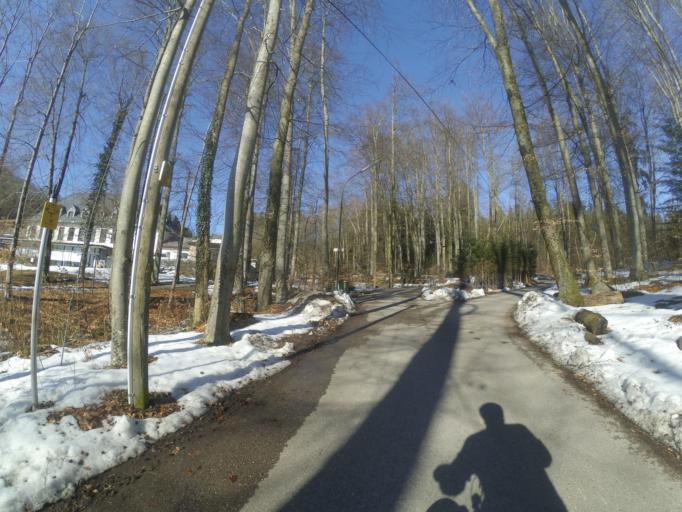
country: DE
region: Bavaria
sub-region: Upper Bavaria
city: Feldkirchen-Westerham
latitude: 47.9072
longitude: 11.8318
